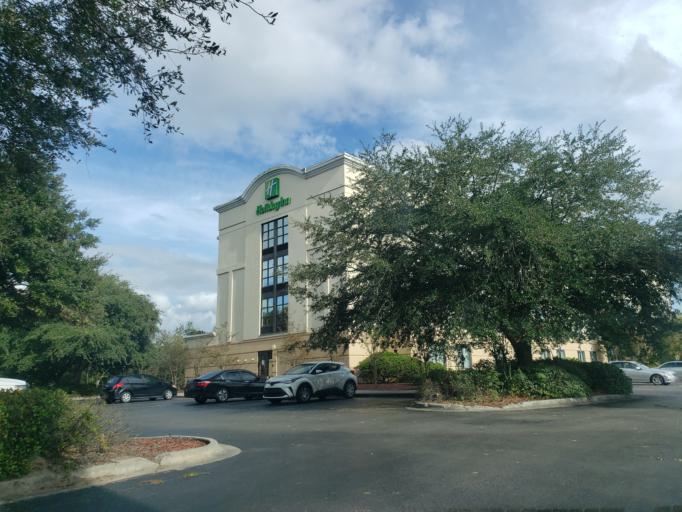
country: US
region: Georgia
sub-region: Chatham County
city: Georgetown
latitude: 32.0073
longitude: -81.2795
